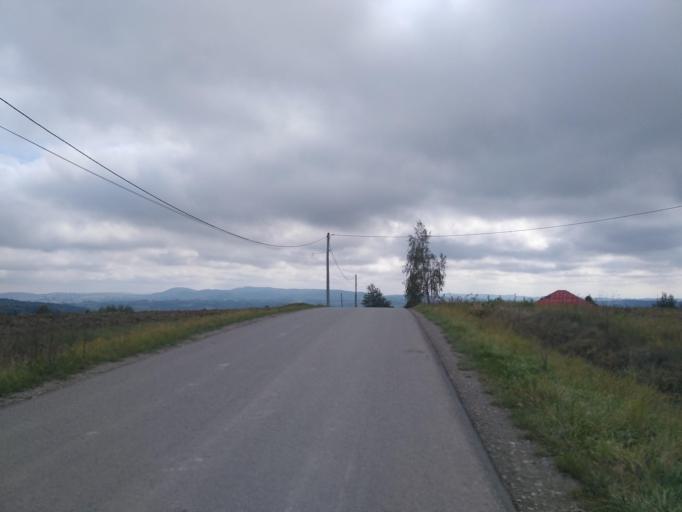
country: PL
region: Subcarpathian Voivodeship
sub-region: Powiat ropczycko-sedziszowski
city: Niedzwiada
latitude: 49.9600
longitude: 21.4522
